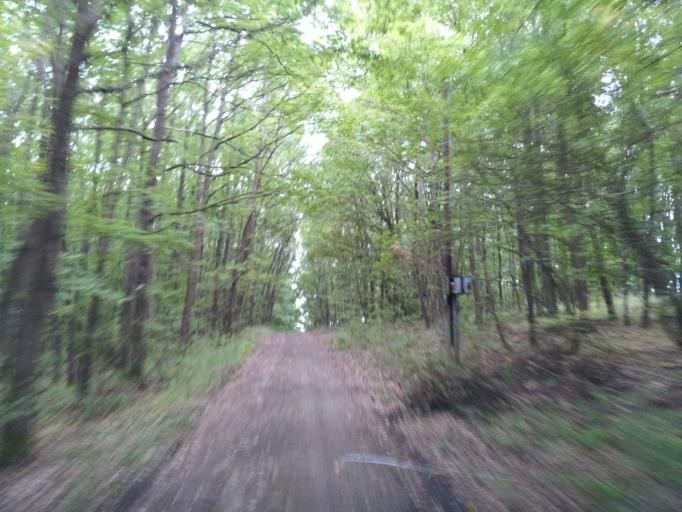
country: HU
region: Pest
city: Kismaros
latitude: 47.8799
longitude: 18.9425
